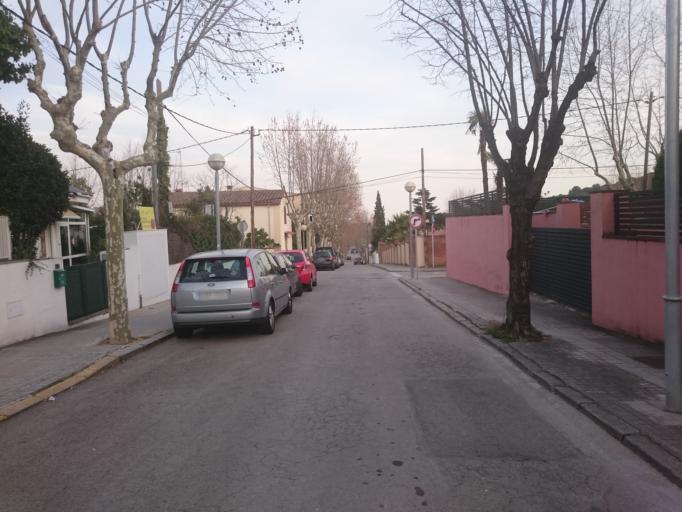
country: ES
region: Catalonia
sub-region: Provincia de Barcelona
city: Argentona
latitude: 41.5510
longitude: 2.3988
